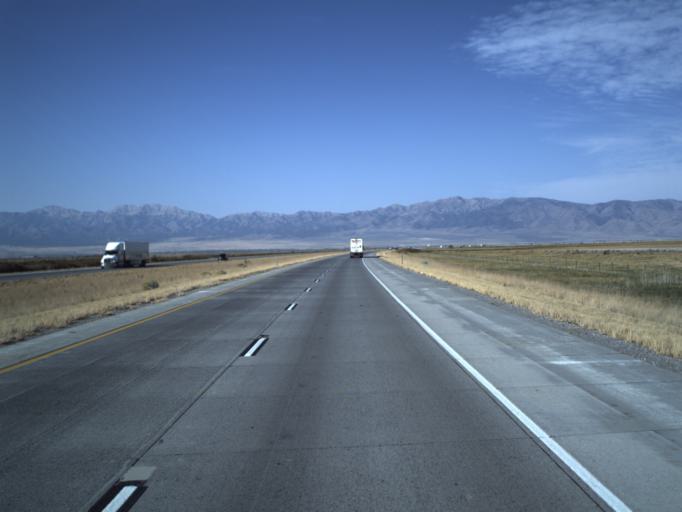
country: US
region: Utah
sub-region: Tooele County
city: Stansbury park
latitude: 40.6676
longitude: -112.3056
